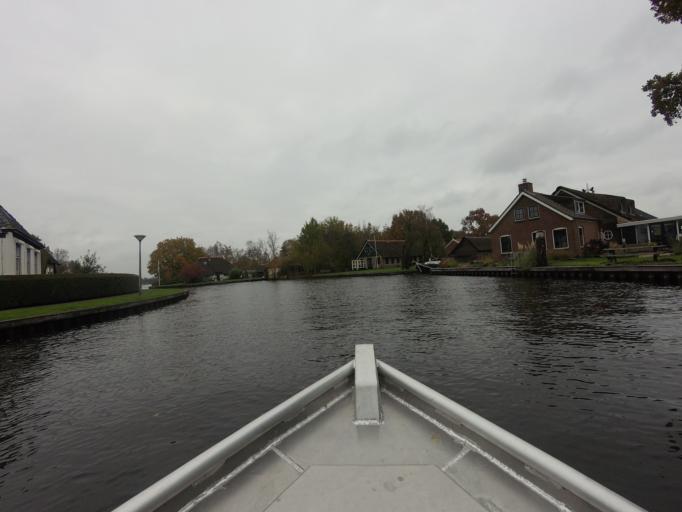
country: NL
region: Overijssel
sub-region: Gemeente Steenwijkerland
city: Oldemarkt
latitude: 52.7787
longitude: 5.9488
